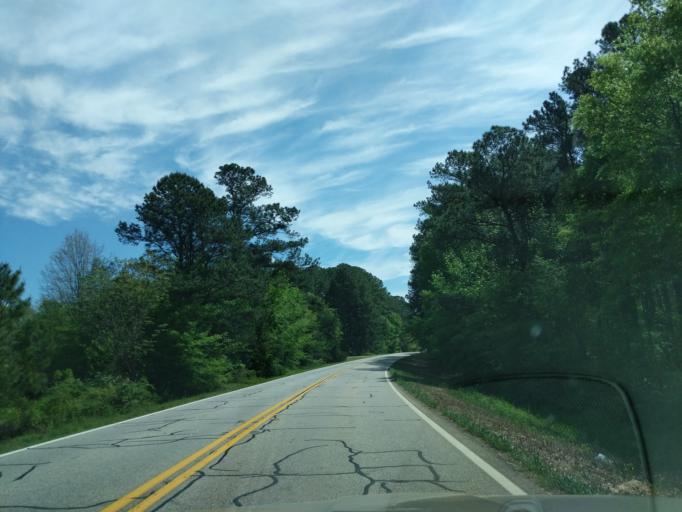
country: US
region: Georgia
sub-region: Columbia County
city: Appling
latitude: 33.6126
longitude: -82.3614
